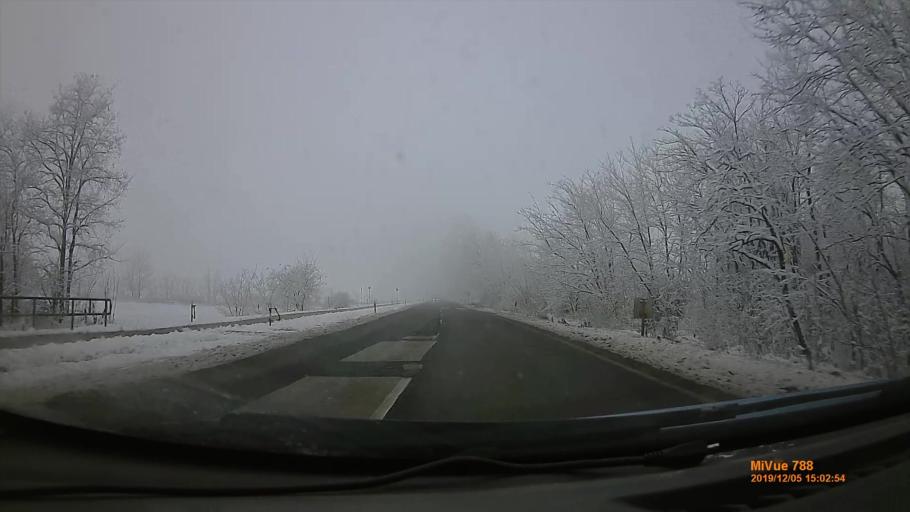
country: HU
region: Szabolcs-Szatmar-Bereg
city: Tiszanagyfalu
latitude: 48.0802
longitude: 21.5069
